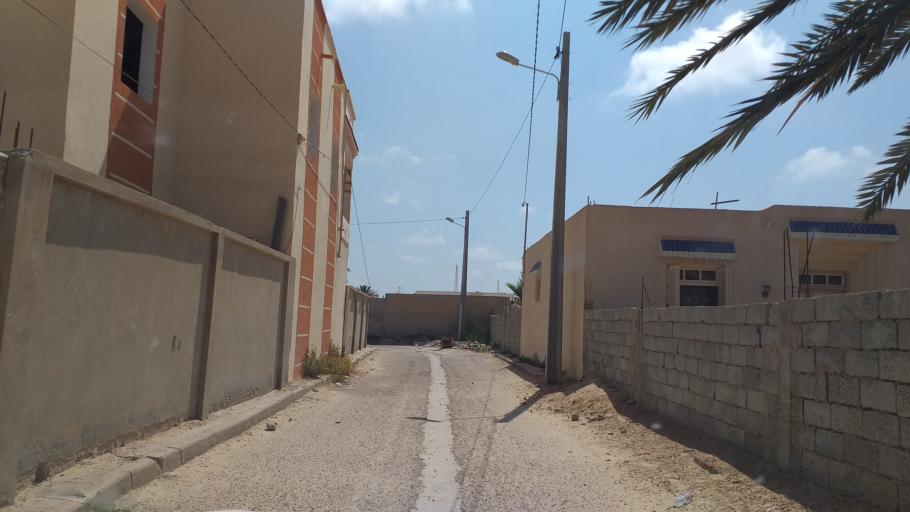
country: TN
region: Qabis
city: Gabes
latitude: 33.9437
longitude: 10.0666
